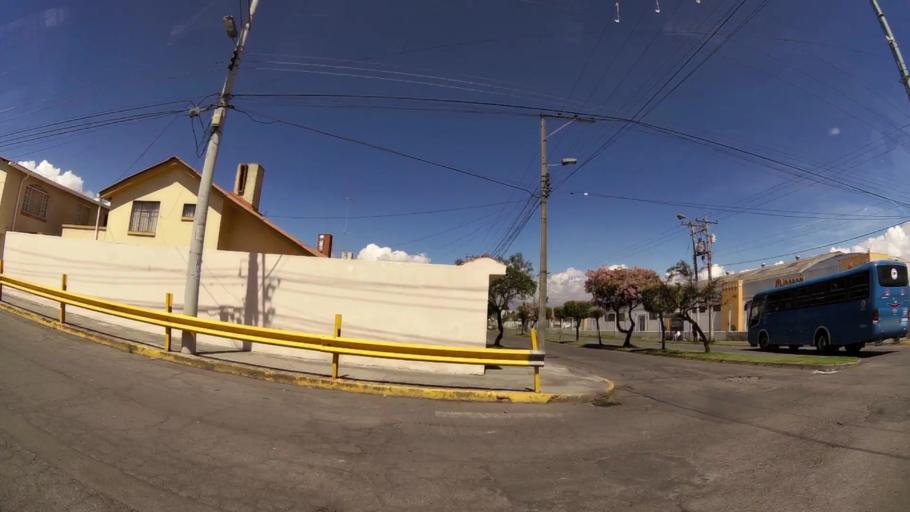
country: EC
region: Chimborazo
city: Riobamba
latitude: -1.6803
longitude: -78.6327
